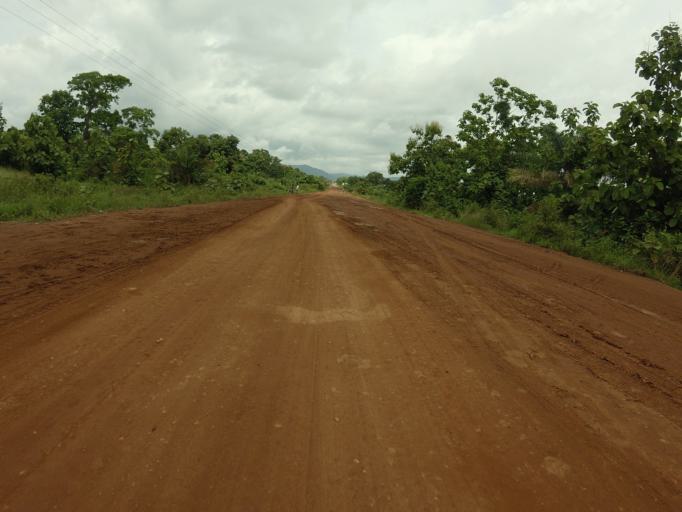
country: GH
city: Kpandae
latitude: 8.2800
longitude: 0.5060
